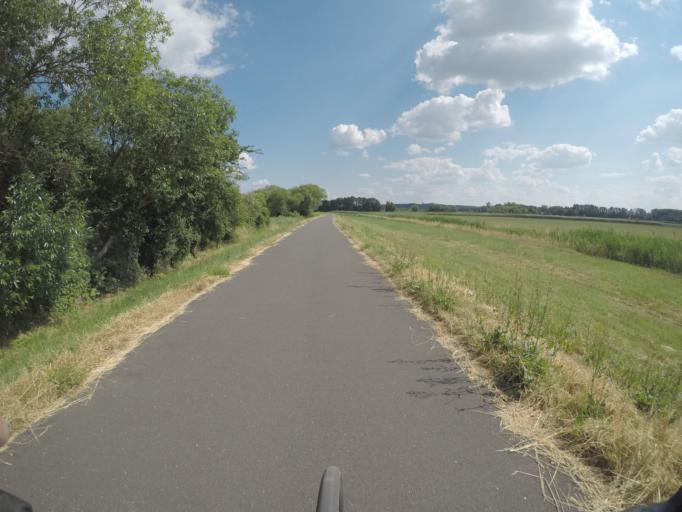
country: DE
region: Brandenburg
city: Ketzin
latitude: 52.4458
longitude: 12.8745
